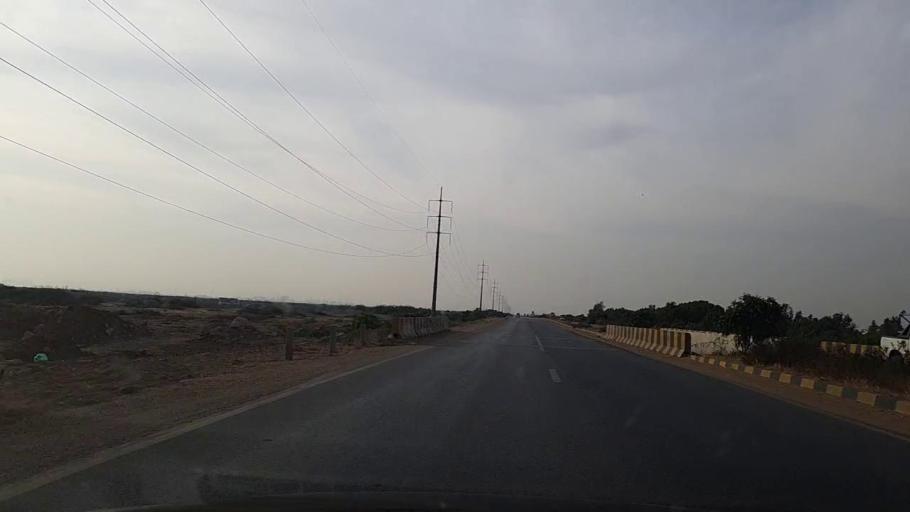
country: PK
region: Sindh
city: Gharo
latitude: 24.8229
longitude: 67.4793
